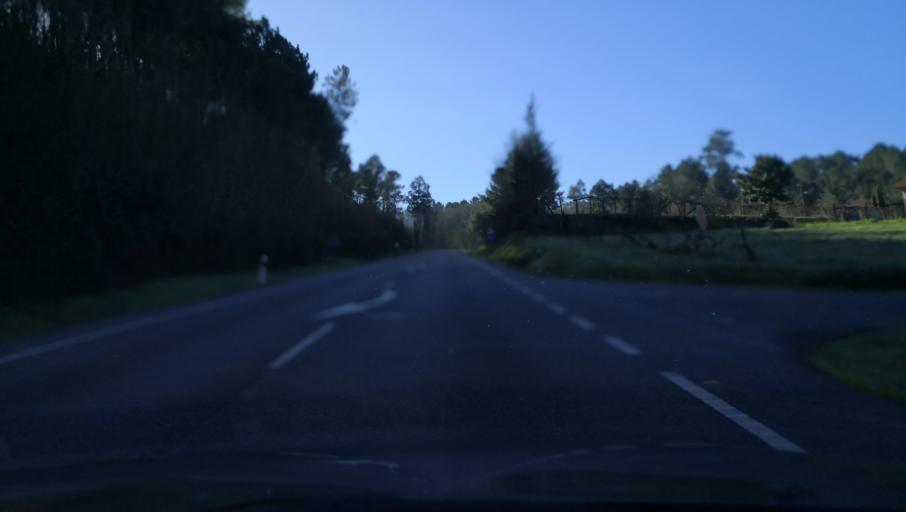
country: ES
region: Galicia
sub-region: Provincia da Coruna
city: Ribeira
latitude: 42.7690
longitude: -8.3981
